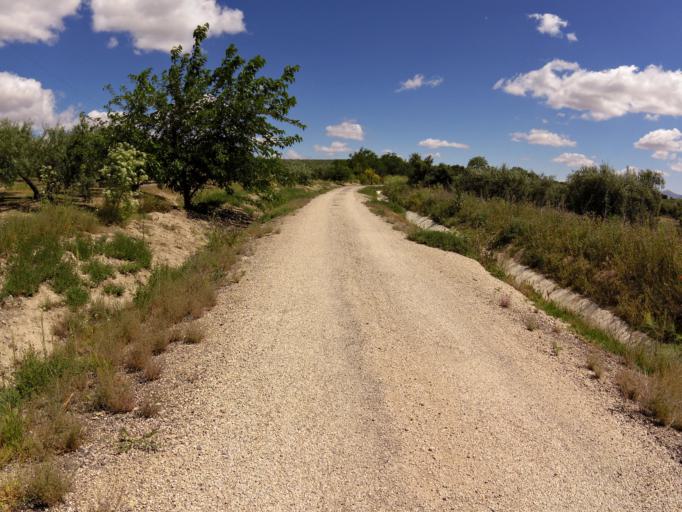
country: ES
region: Andalusia
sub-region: Provincia de Jaen
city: Alcaudete
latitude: 37.6617
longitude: -4.0622
